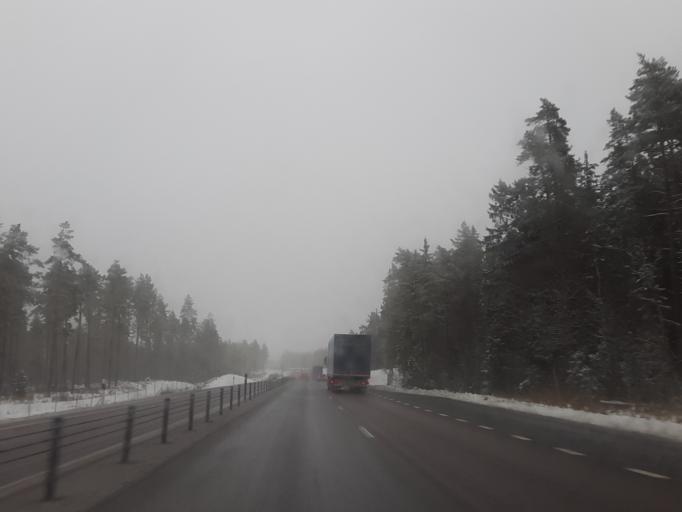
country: SE
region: Joenkoeping
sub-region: Jonkopings Kommun
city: Taberg
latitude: 57.7564
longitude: 13.9951
